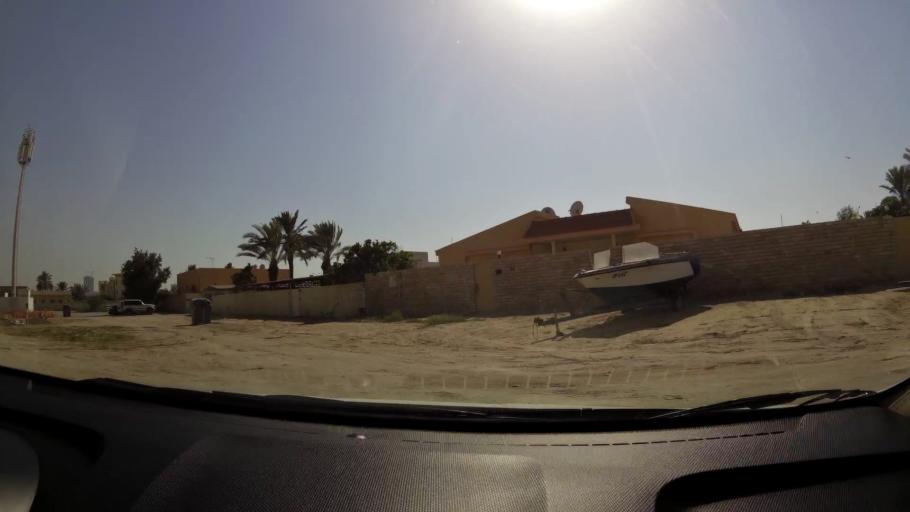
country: AE
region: Ajman
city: Ajman
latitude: 25.4105
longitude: 55.4675
